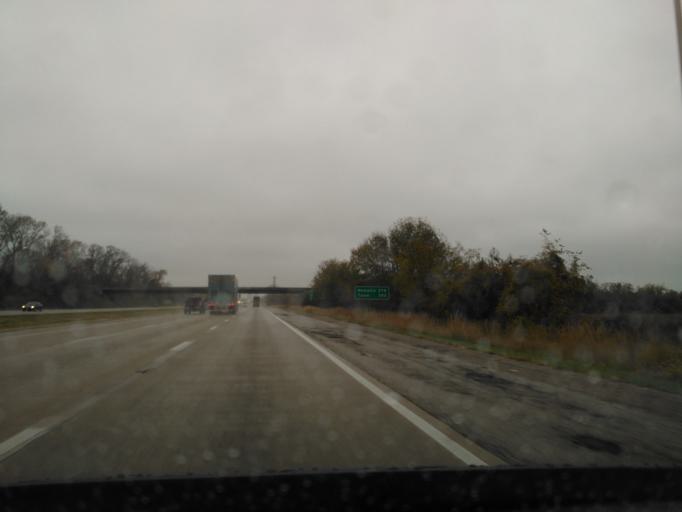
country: US
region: Illinois
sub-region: Saint Clair County
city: Dupo
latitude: 38.4777
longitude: -90.2447
